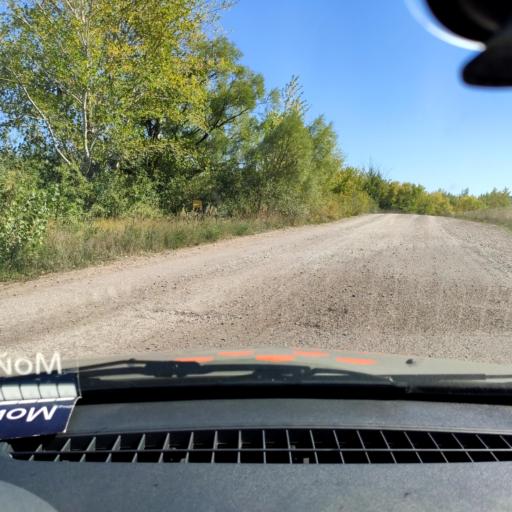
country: RU
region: Bashkortostan
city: Yermolayevo
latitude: 52.7527
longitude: 55.8260
